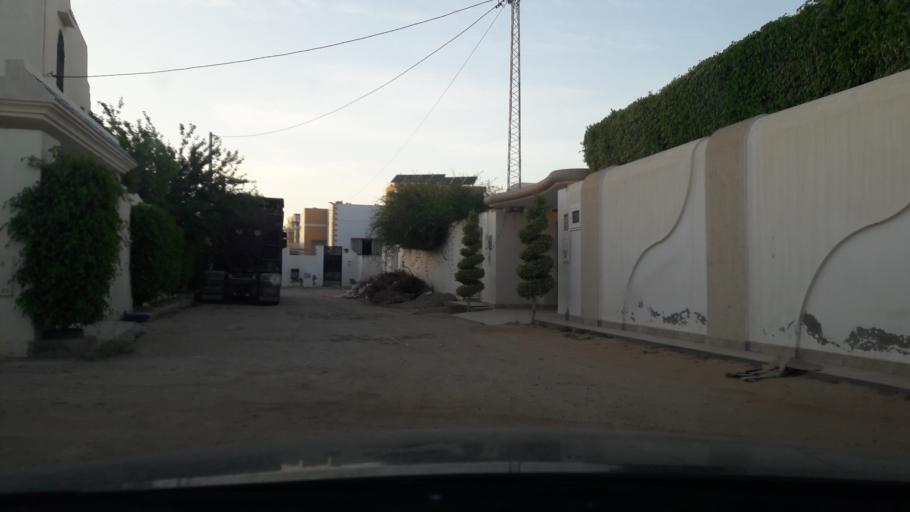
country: TN
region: Safaqis
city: Al Qarmadah
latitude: 34.7954
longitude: 10.7550
